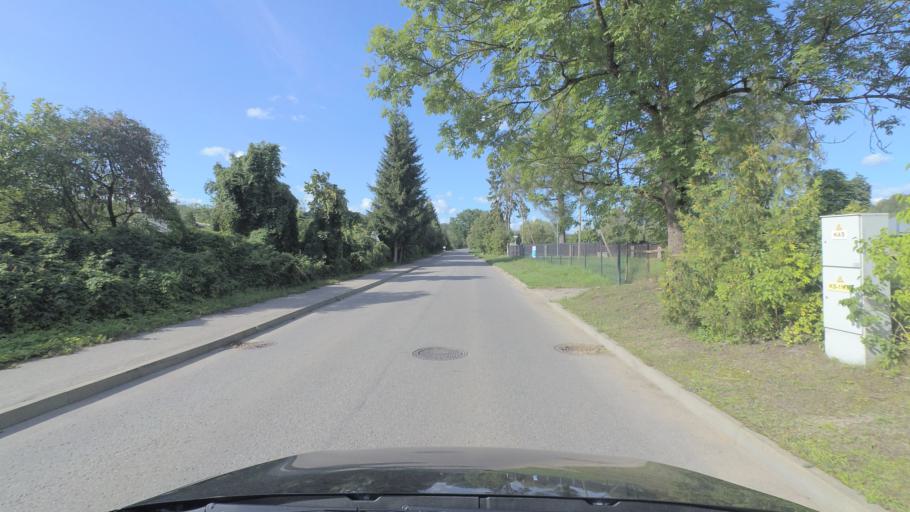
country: LT
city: Nemencine
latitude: 54.8370
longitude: 25.3707
